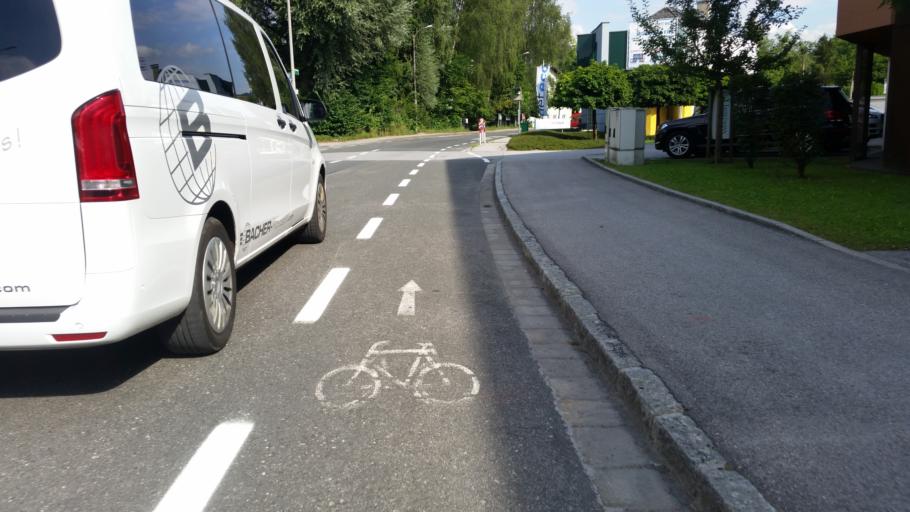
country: AT
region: Salzburg
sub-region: Salzburg Stadt
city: Salzburg
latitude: 47.7809
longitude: 13.0550
